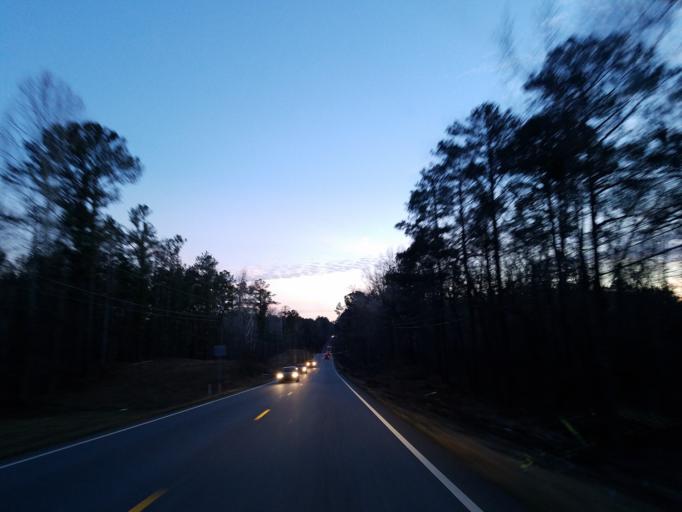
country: US
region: Georgia
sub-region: Paulding County
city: Dallas
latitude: 33.9462
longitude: -84.8474
